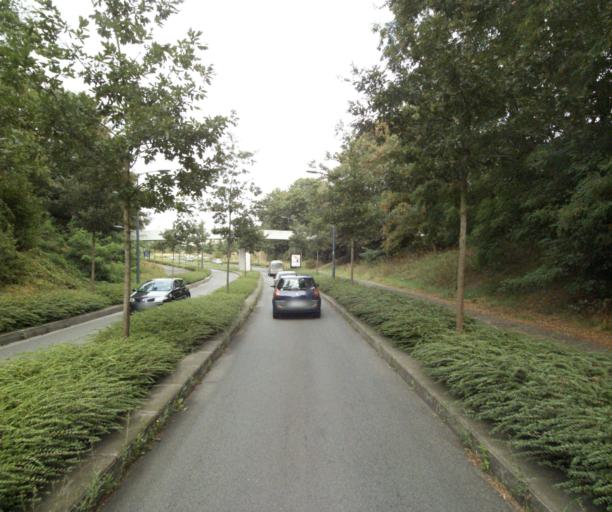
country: FR
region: Nord-Pas-de-Calais
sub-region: Departement du Nord
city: Villeneuve-d'Ascq
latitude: 50.6158
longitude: 3.1442
